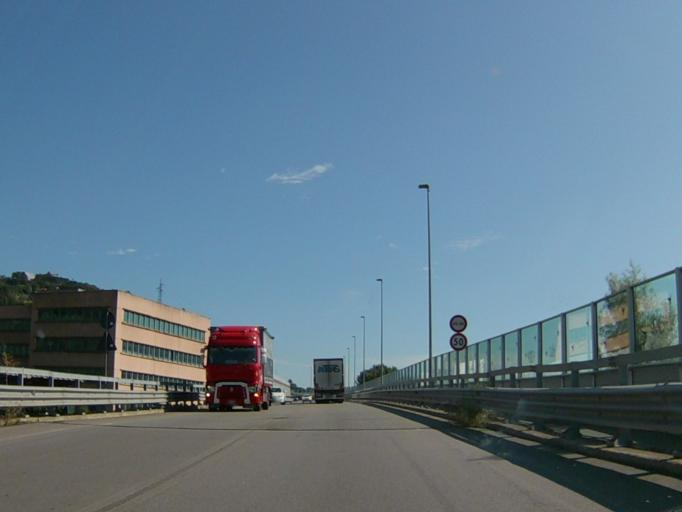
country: IT
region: Lombardy
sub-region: Provincia di Lecco
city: Vercurago
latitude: 45.8221
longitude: 9.4152
